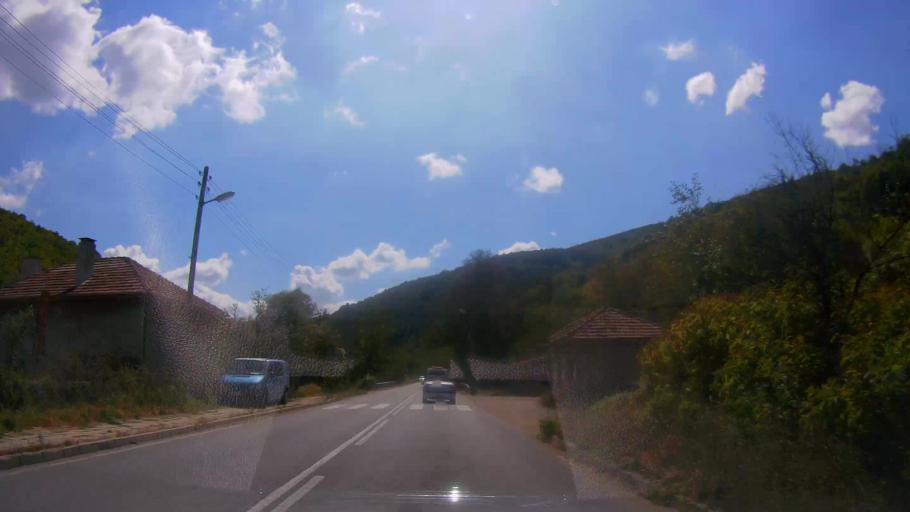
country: BG
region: Stara Zagora
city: Gurkovo
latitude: 42.7392
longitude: 25.7080
